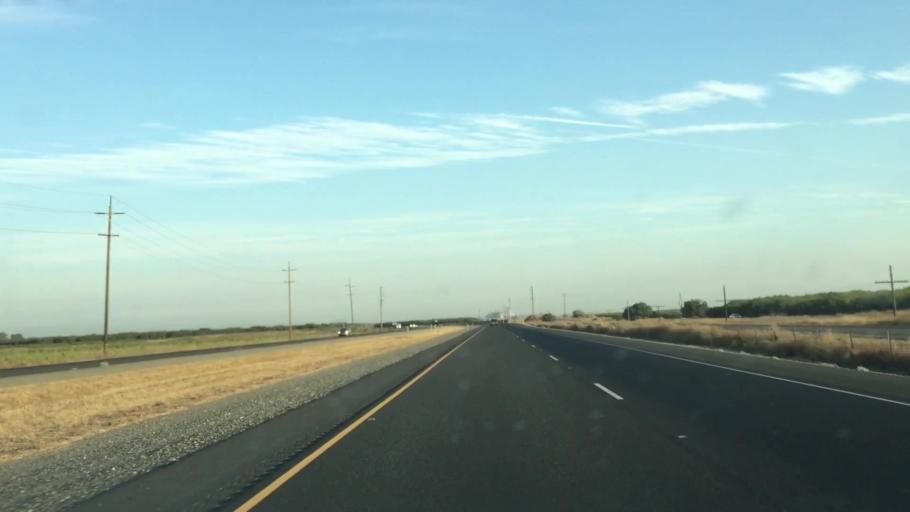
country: US
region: California
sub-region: Colusa County
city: Arbuckle
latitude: 39.0466
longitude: -122.0761
